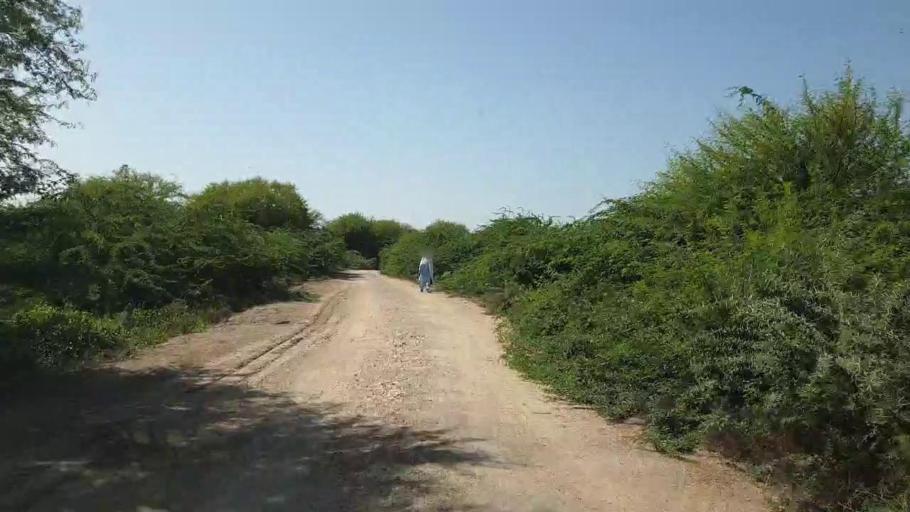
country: PK
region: Sindh
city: Tando Bago
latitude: 24.7068
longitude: 69.0468
